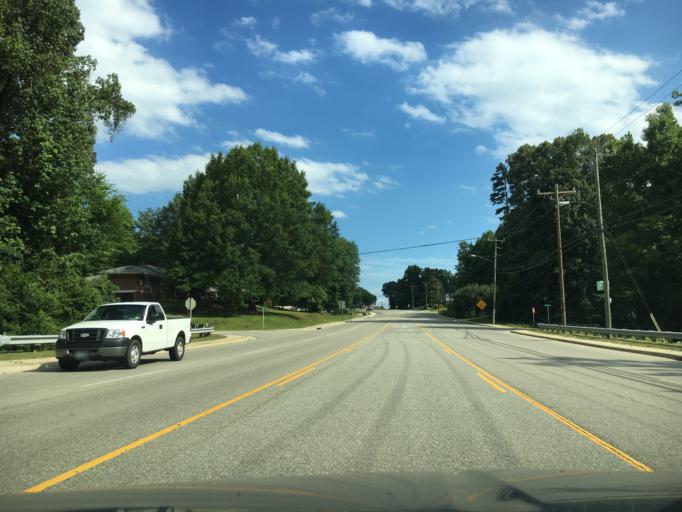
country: US
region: Virginia
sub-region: Halifax County
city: South Boston
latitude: 36.7110
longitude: -78.9122
